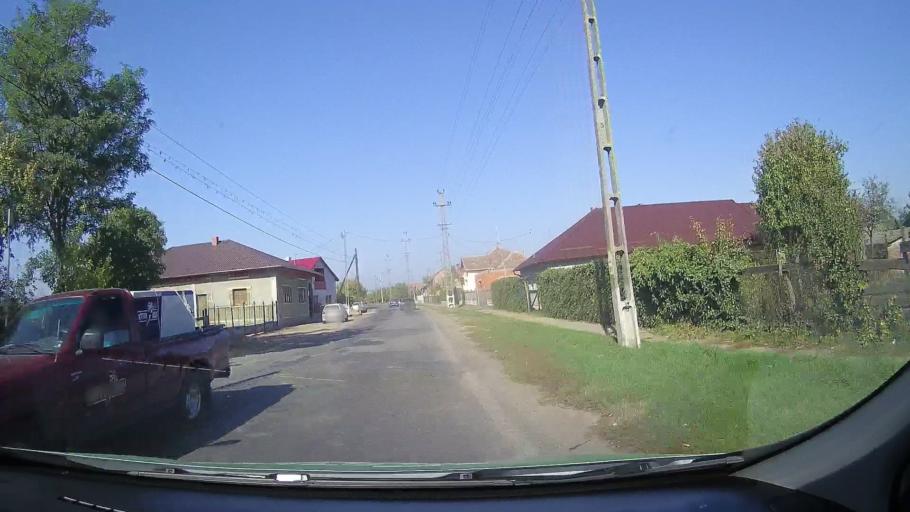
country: RO
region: Satu Mare
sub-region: Comuna Sanislau
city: Sanislau
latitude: 47.6314
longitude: 22.3316
